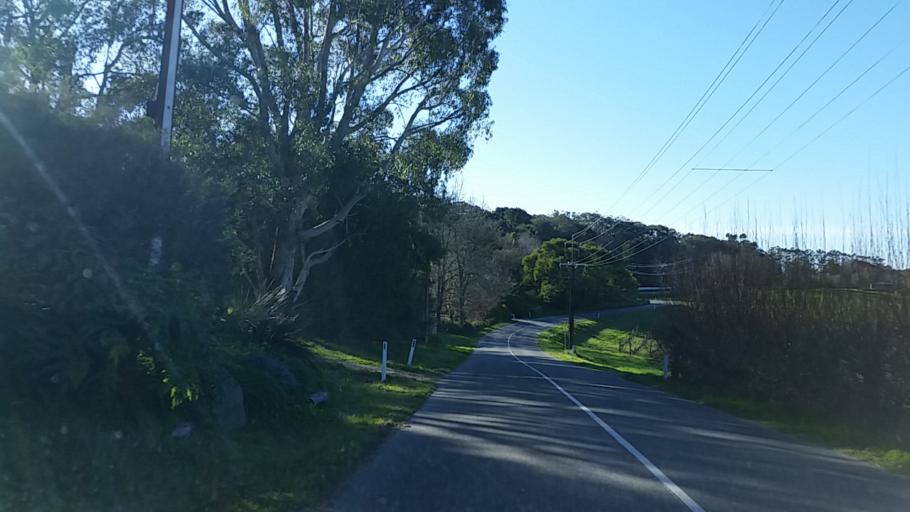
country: AU
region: South Australia
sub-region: Adelaide Hills
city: Adelaide Hills
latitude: -34.9518
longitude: 138.7220
